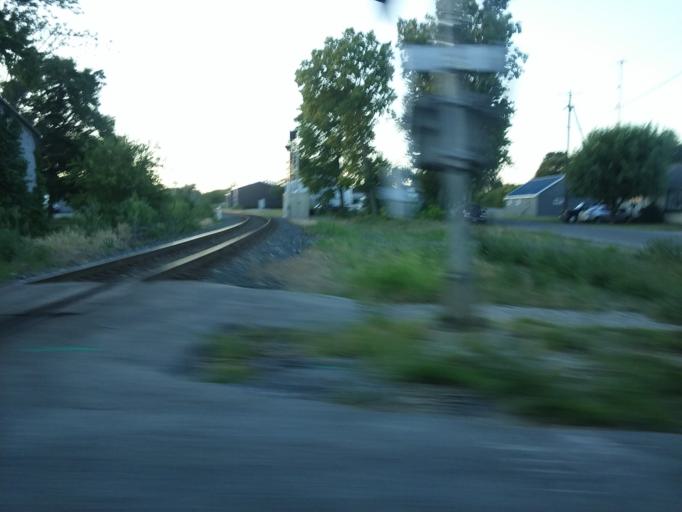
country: US
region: Ohio
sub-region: Hancock County
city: Findlay
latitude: 41.0454
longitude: -83.6443
